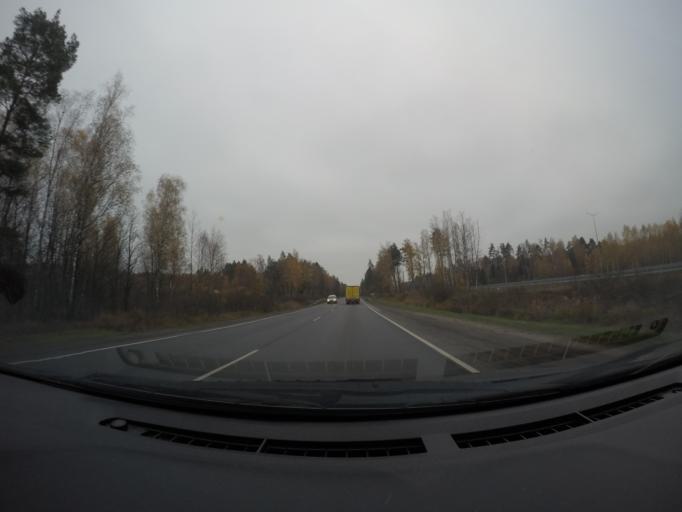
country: RU
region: Moskovskaya
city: Gzhel'
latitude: 55.5677
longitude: 38.3933
